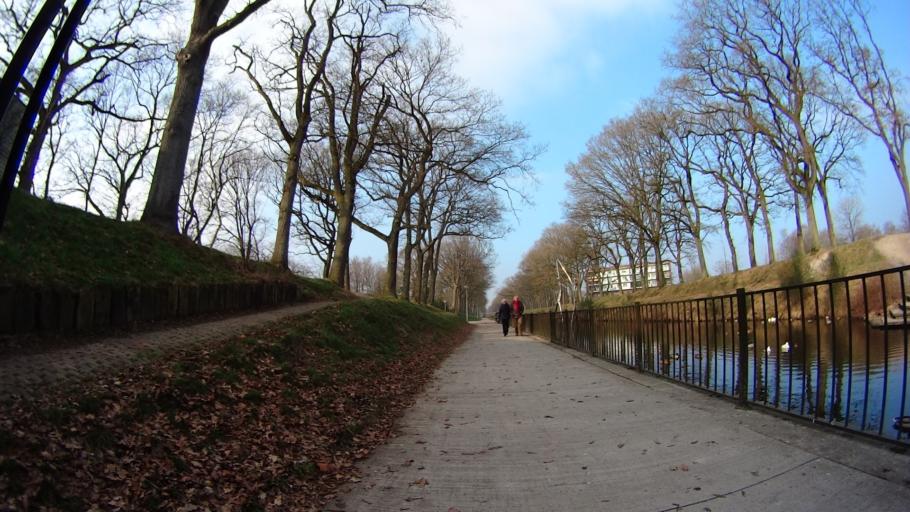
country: NL
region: Drenthe
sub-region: Gemeente Emmen
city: Emmen
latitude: 52.7648
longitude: 6.8870
